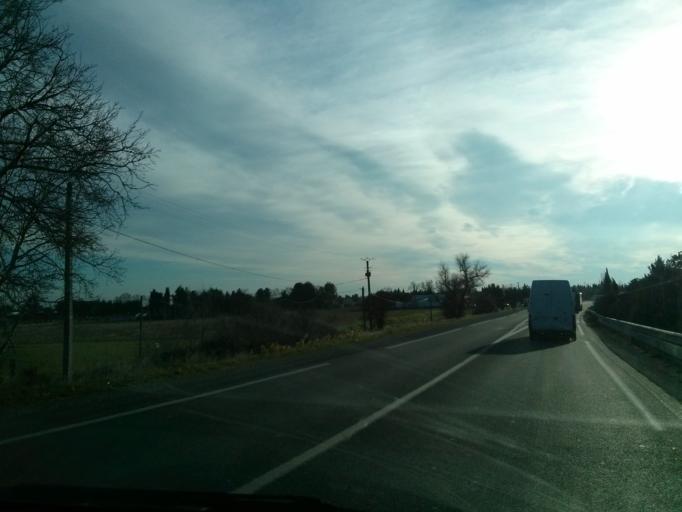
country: FR
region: Languedoc-Roussillon
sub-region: Departement de l'Herault
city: Lunel
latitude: 43.6759
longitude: 4.1498
